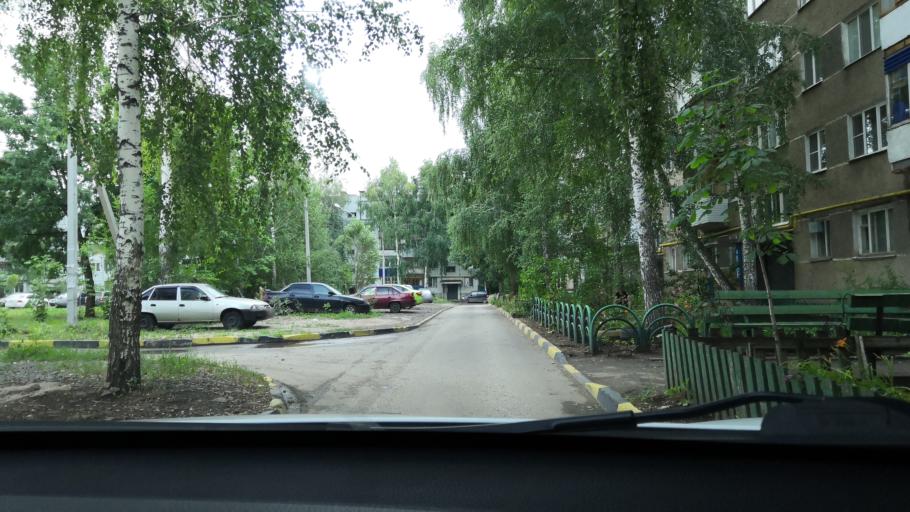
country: RU
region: Samara
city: Smyshlyayevka
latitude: 53.2701
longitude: 50.3871
